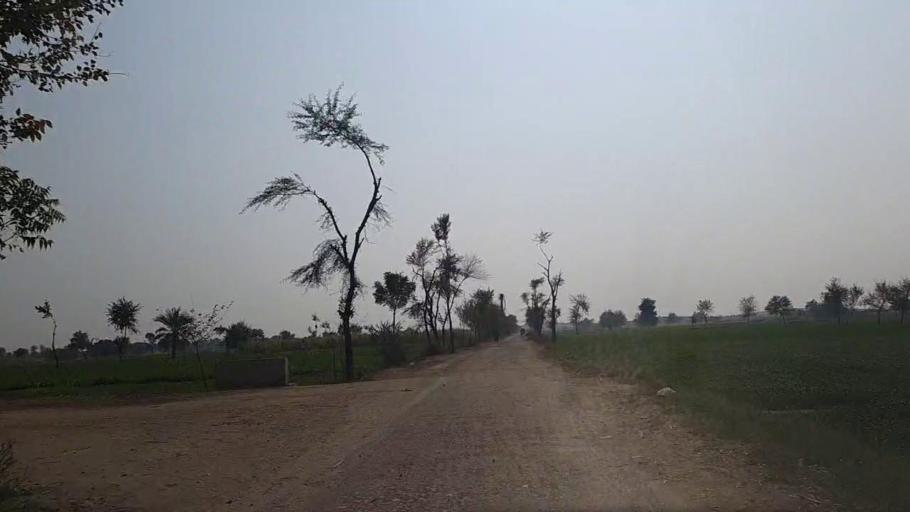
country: PK
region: Sindh
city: Jam Sahib
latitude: 26.4556
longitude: 68.5235
